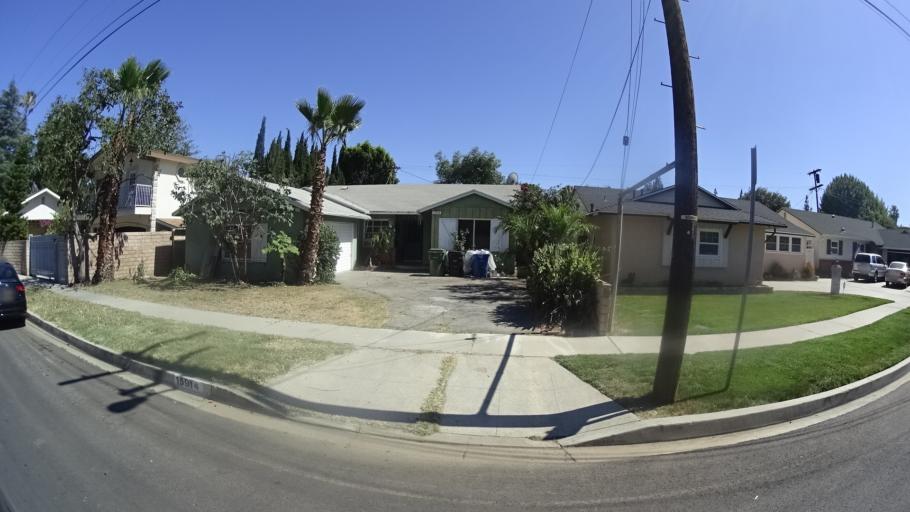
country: US
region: California
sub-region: Los Angeles County
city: Van Nuys
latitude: 34.1878
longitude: -118.4799
